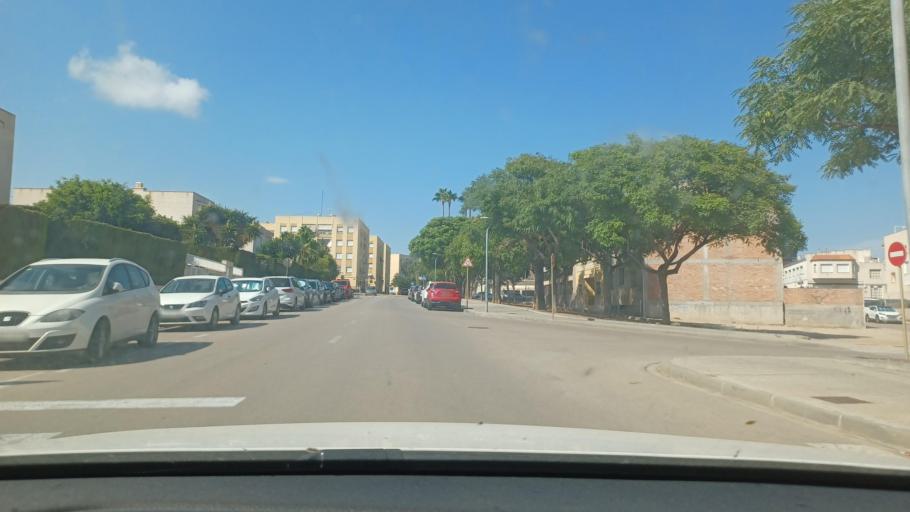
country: ES
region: Catalonia
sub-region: Provincia de Tarragona
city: Sant Carles de la Rapita
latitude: 40.6137
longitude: 0.5833
